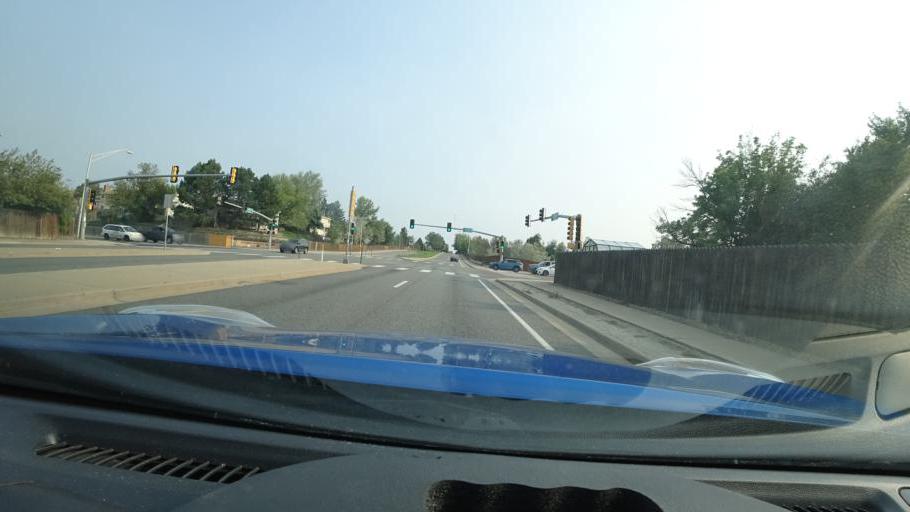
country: US
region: Colorado
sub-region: Adams County
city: Aurora
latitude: 39.6680
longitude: -104.7912
